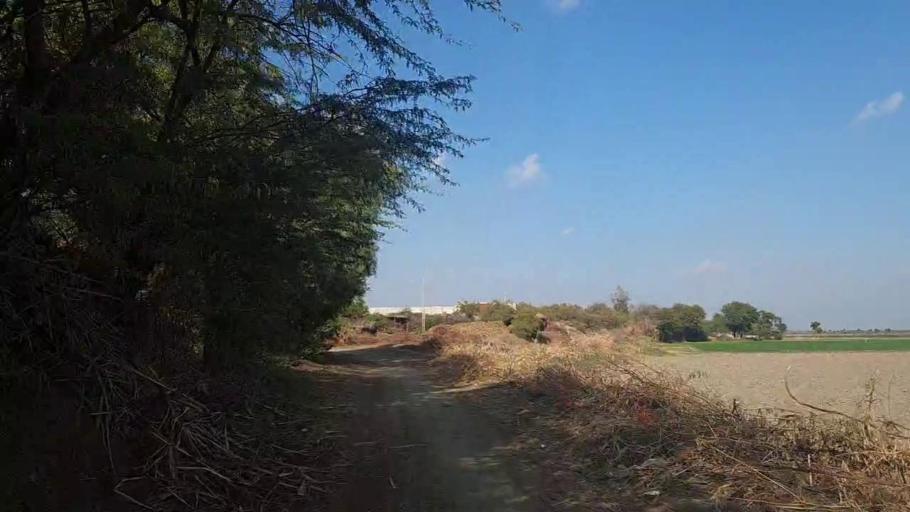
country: PK
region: Sindh
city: Tando Mittha Khan
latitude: 25.9949
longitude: 69.2441
